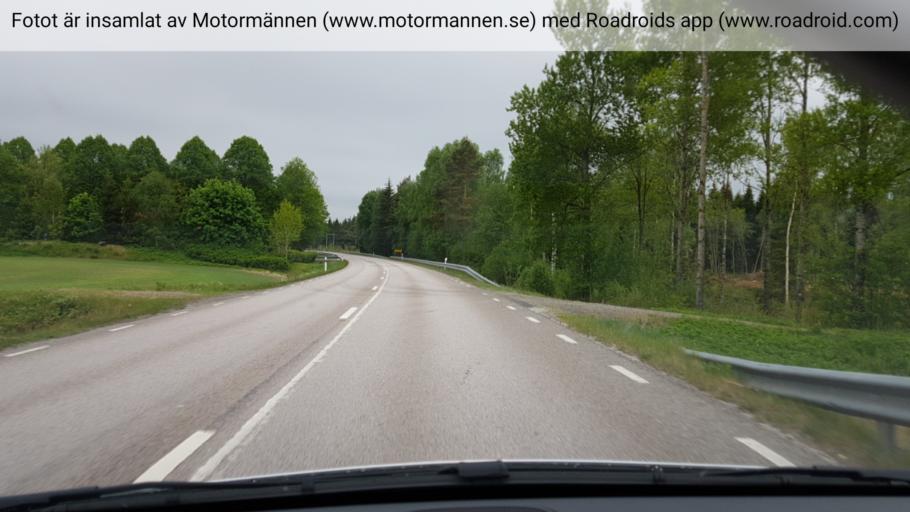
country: SE
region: Vaestra Goetaland
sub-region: Tidaholms Kommun
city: Tidaholm
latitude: 58.0743
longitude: 13.8645
